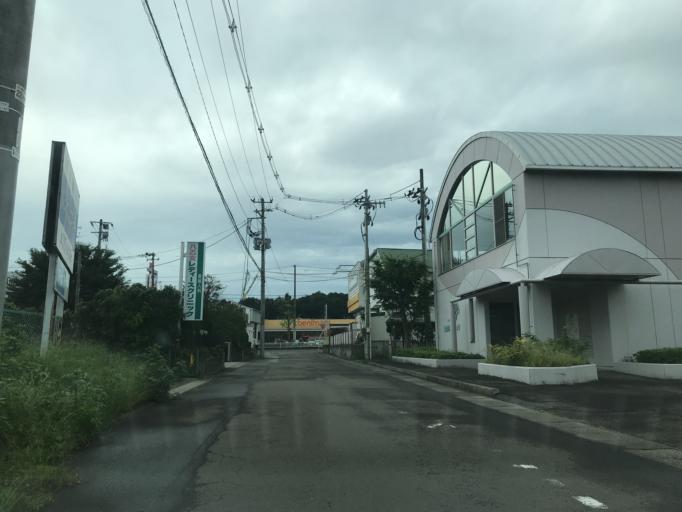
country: JP
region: Miyagi
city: Sendai-shi
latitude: 38.3167
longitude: 140.8725
